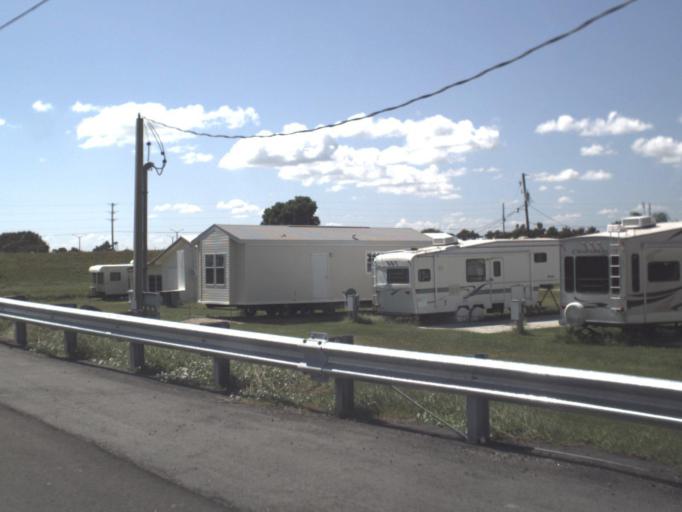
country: US
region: Florida
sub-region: Glades County
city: Buckhead Ridge
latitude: 27.1538
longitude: -80.8668
